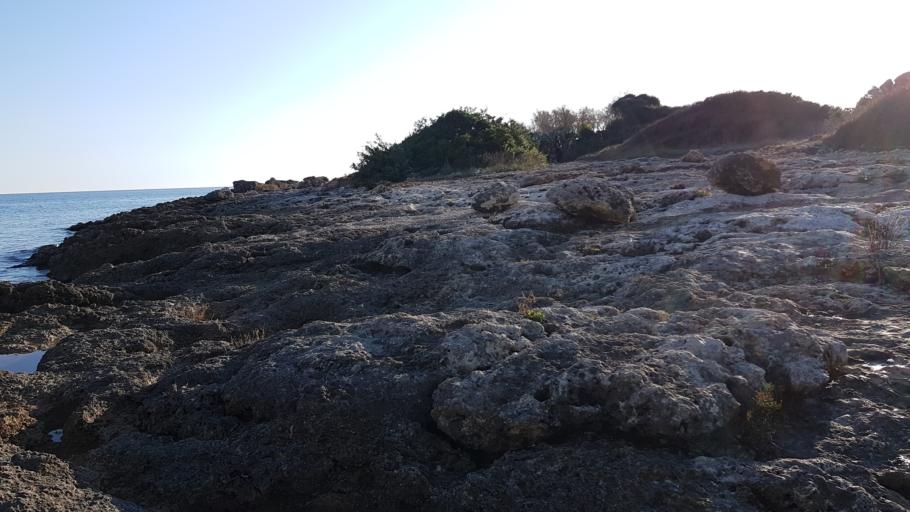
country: IT
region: Apulia
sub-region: Provincia di Taranto
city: Avetrana
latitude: 40.2930
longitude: 17.7666
